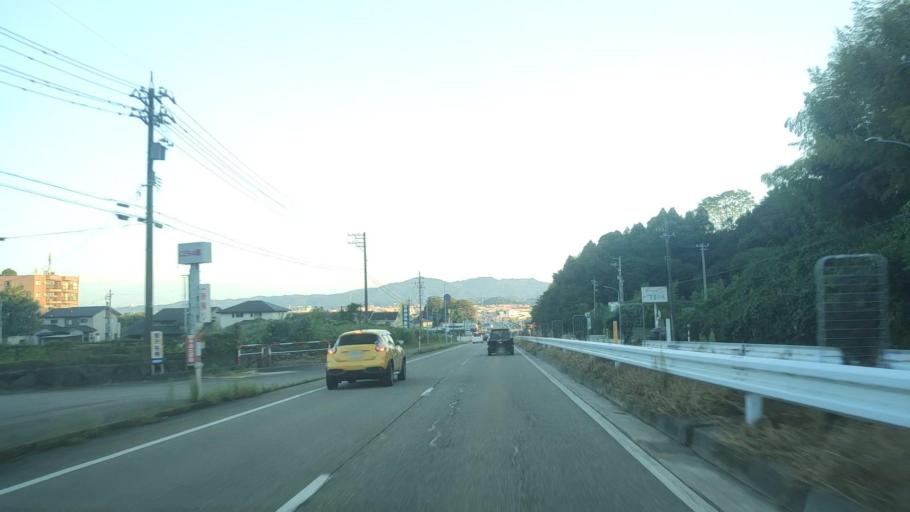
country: JP
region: Toyama
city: Himi
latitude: 36.8490
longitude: 136.9793
